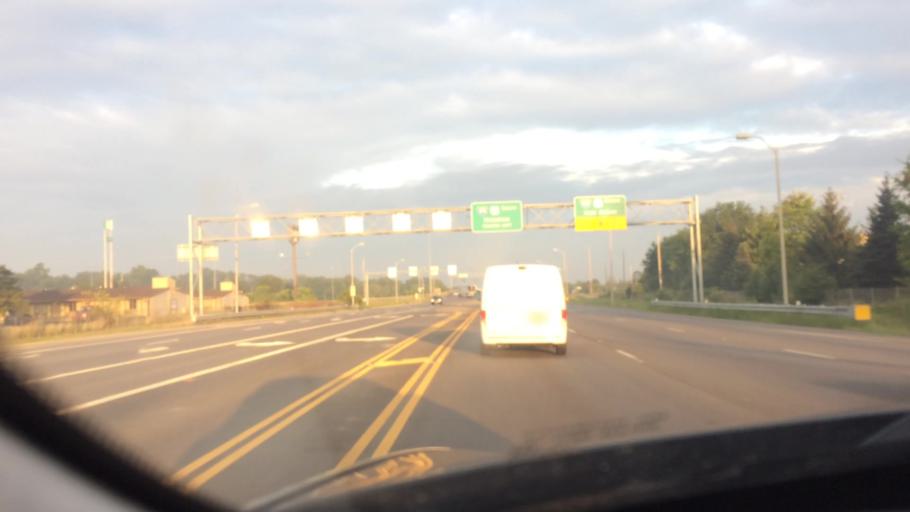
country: US
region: Ohio
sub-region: Lucas County
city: Holland
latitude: 41.6137
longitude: -83.6853
